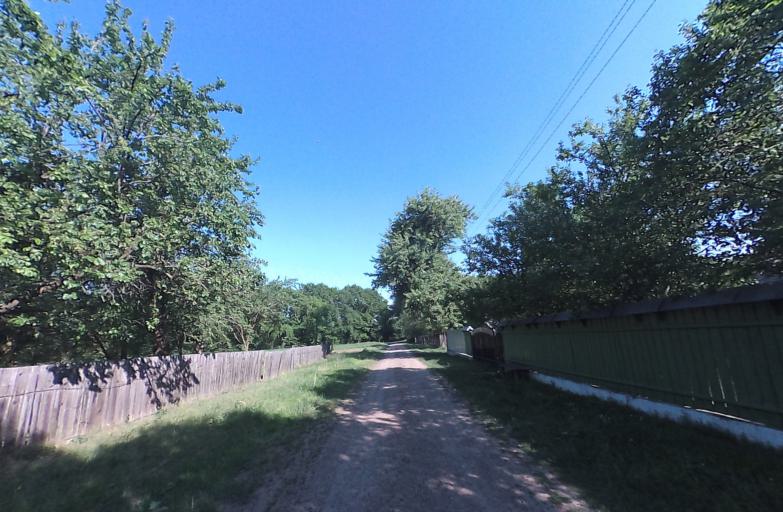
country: RO
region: Neamt
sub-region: Comuna Dulcesti
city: Dulcesti
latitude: 46.9973
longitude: 26.7826
